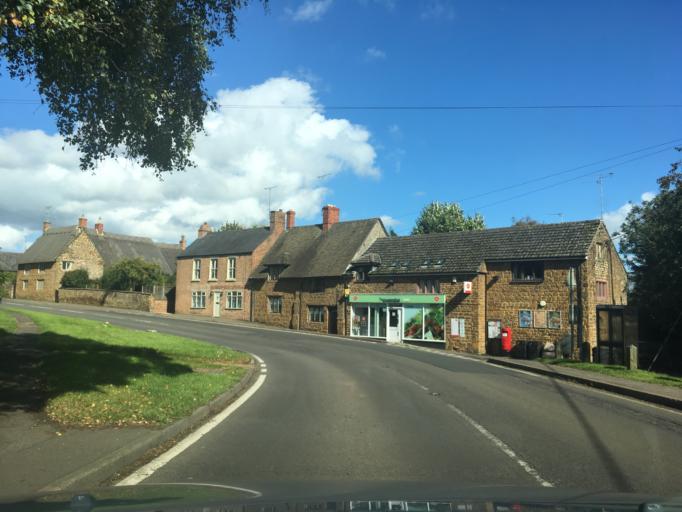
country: GB
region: England
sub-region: Oxfordshire
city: Claydon
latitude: 52.1742
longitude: -1.2457
